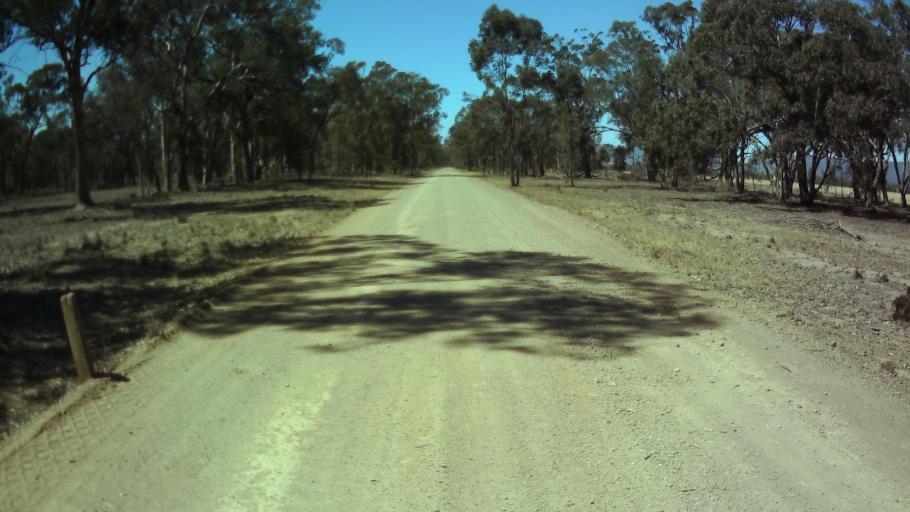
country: AU
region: New South Wales
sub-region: Weddin
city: Grenfell
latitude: -33.8515
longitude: 148.0882
